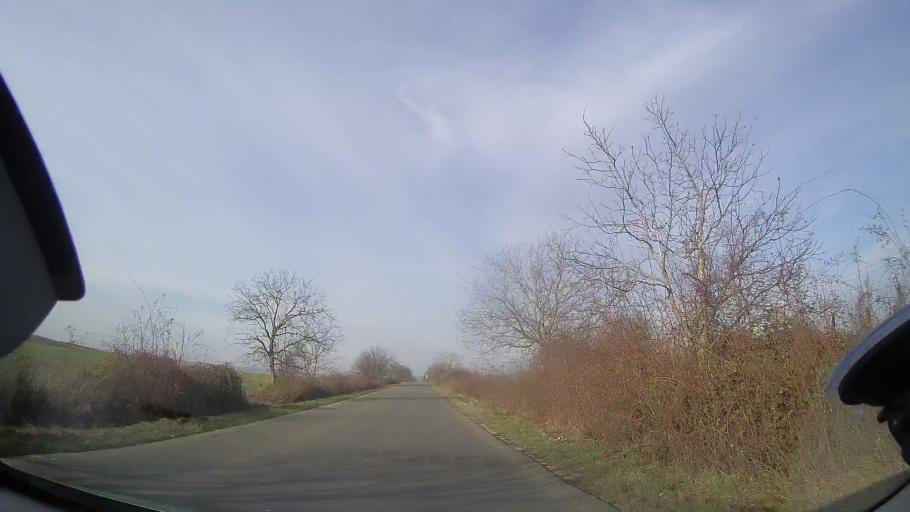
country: RO
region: Bihor
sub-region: Comuna Spinus
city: Spinus
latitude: 47.2182
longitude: 22.1736
